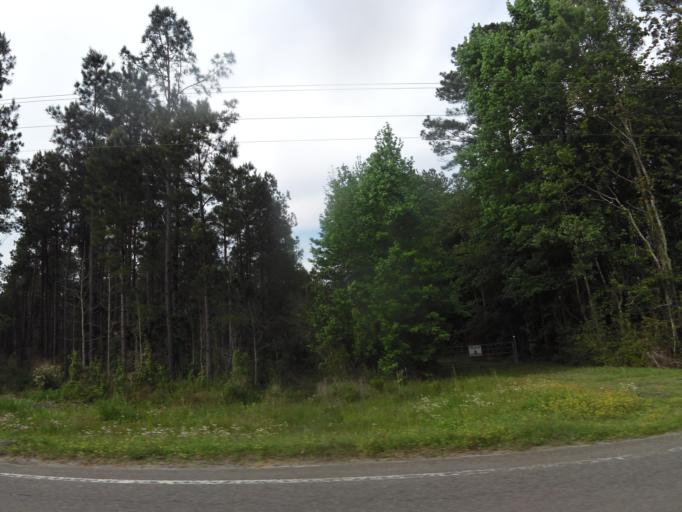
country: US
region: Florida
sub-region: Nassau County
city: Hilliard
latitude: 30.6945
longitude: -81.8372
